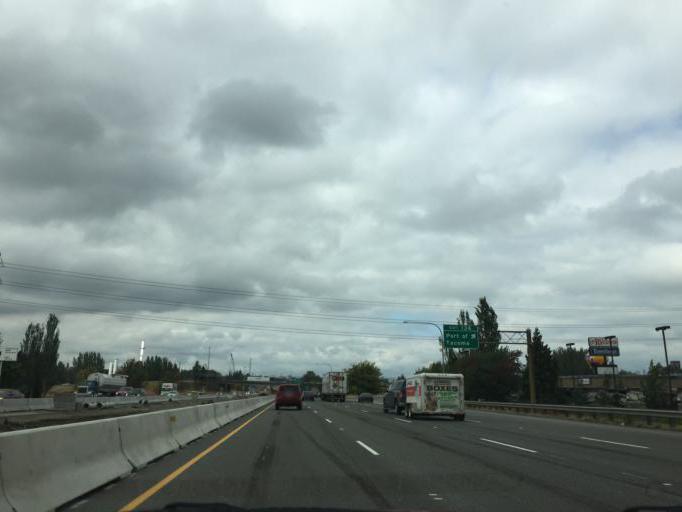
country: US
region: Washington
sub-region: Pierce County
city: Fife
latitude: 47.2409
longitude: -122.3798
